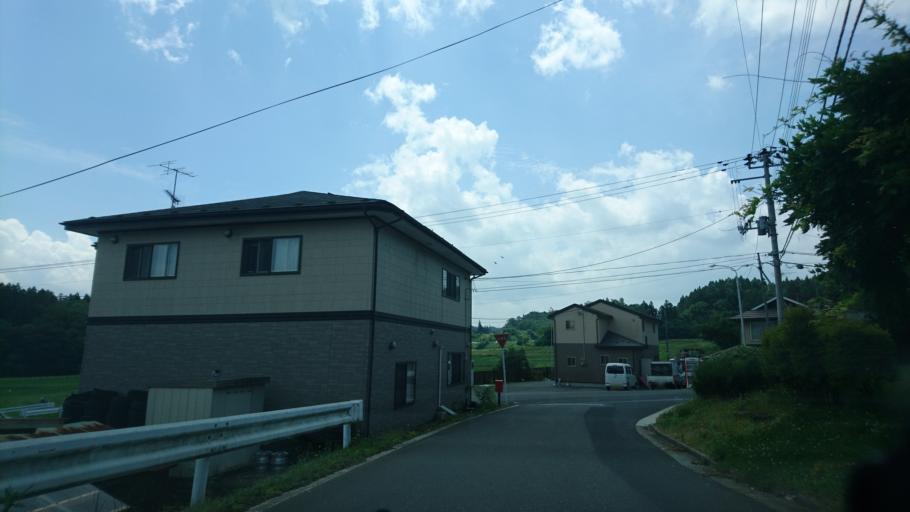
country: JP
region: Iwate
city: Ichinoseki
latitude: 38.9071
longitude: 141.2237
